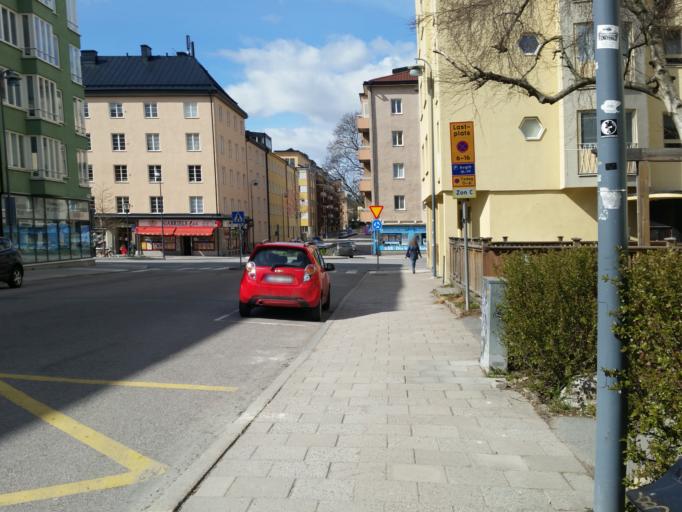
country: SE
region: Stockholm
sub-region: Sundbybergs Kommun
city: Sundbyberg
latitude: 59.3651
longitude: 17.9642
